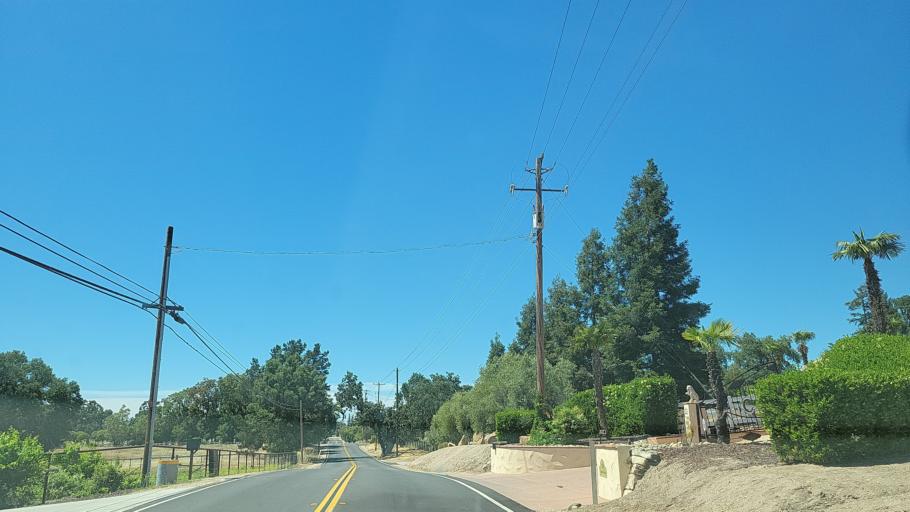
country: US
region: California
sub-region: San Luis Obispo County
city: Atascadero
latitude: 35.5002
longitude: -120.6484
